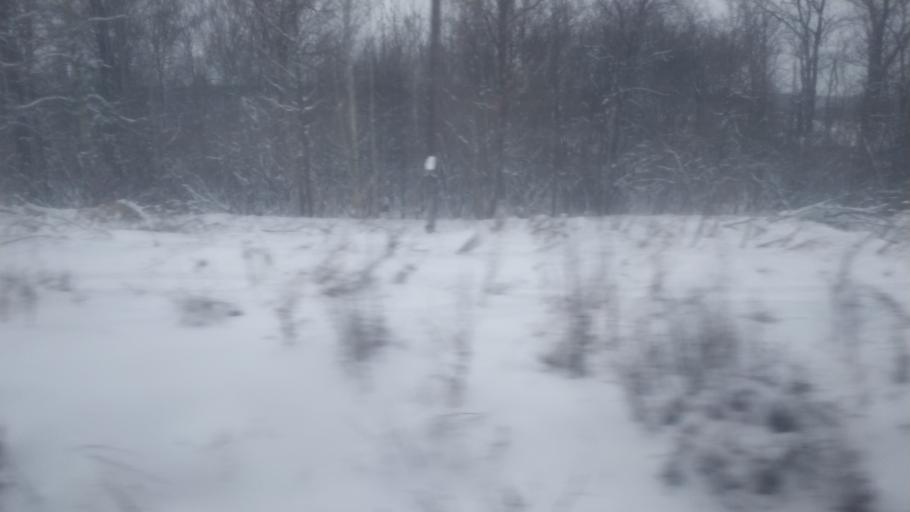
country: RU
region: Udmurtiya
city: Sigayevo
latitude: 56.4525
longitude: 53.7058
